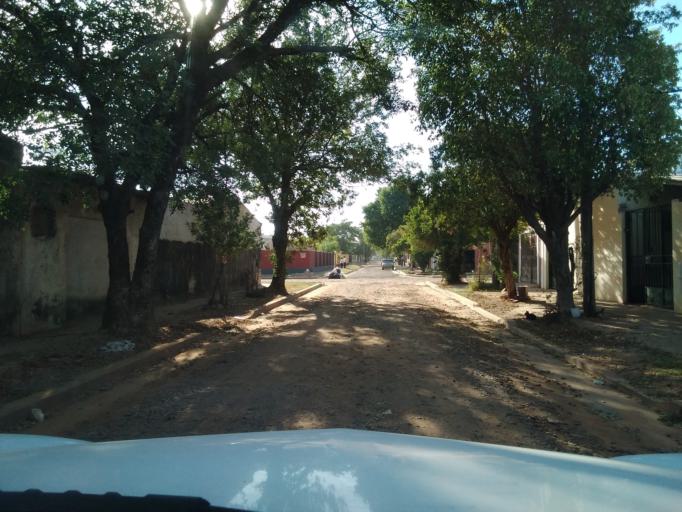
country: AR
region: Corrientes
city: Corrientes
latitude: -27.4910
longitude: -58.7844
